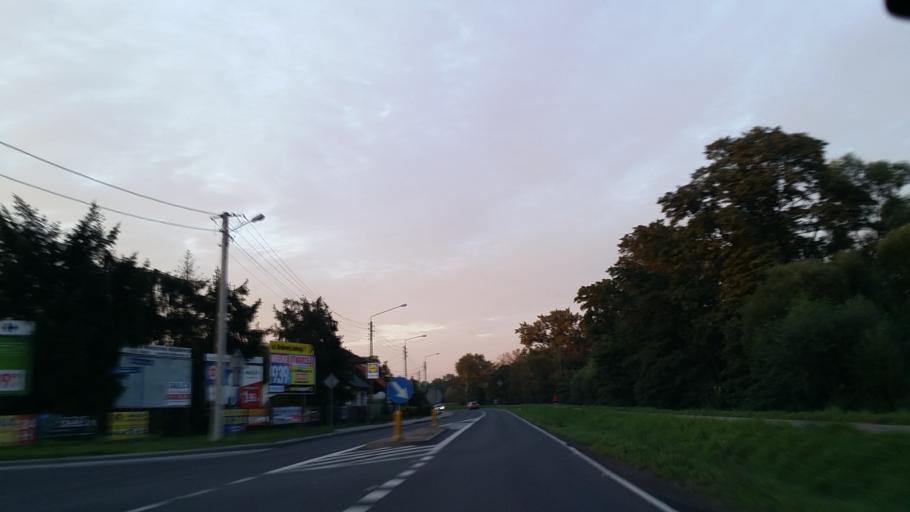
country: PL
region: Lesser Poland Voivodeship
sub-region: Powiat oswiecimski
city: Oswiecim
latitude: 50.0285
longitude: 19.2085
